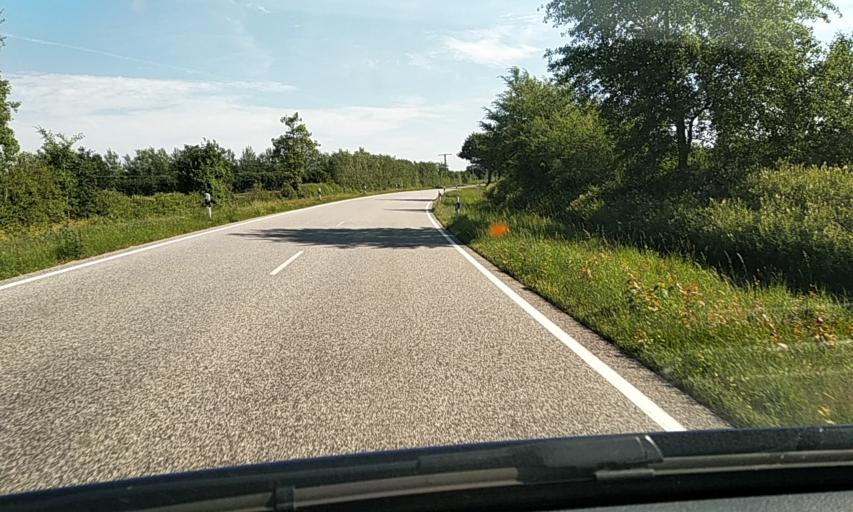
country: DE
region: Schleswig-Holstein
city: Fockbek
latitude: 54.2912
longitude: 9.5824
